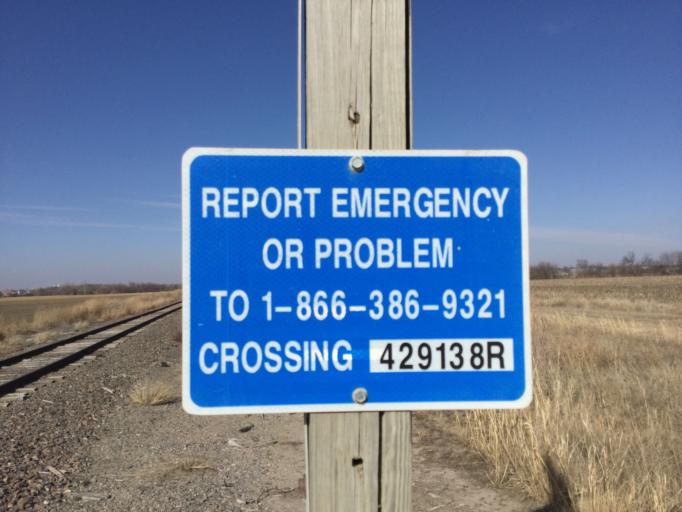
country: US
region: Kansas
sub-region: Rice County
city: Lyons
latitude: 38.3187
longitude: -98.1927
